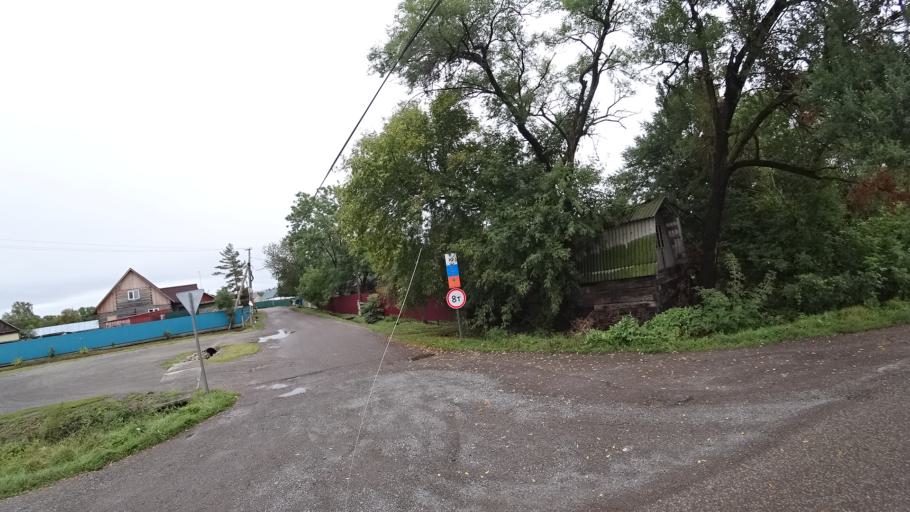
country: RU
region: Primorskiy
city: Monastyrishche
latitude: 44.2036
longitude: 132.4399
